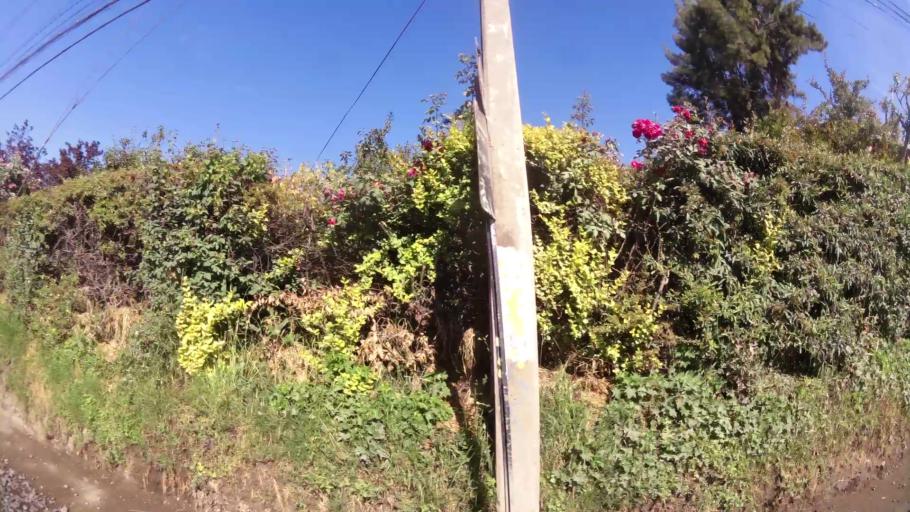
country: CL
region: Santiago Metropolitan
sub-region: Provincia de Maipo
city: San Bernardo
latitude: -33.6176
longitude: -70.6923
